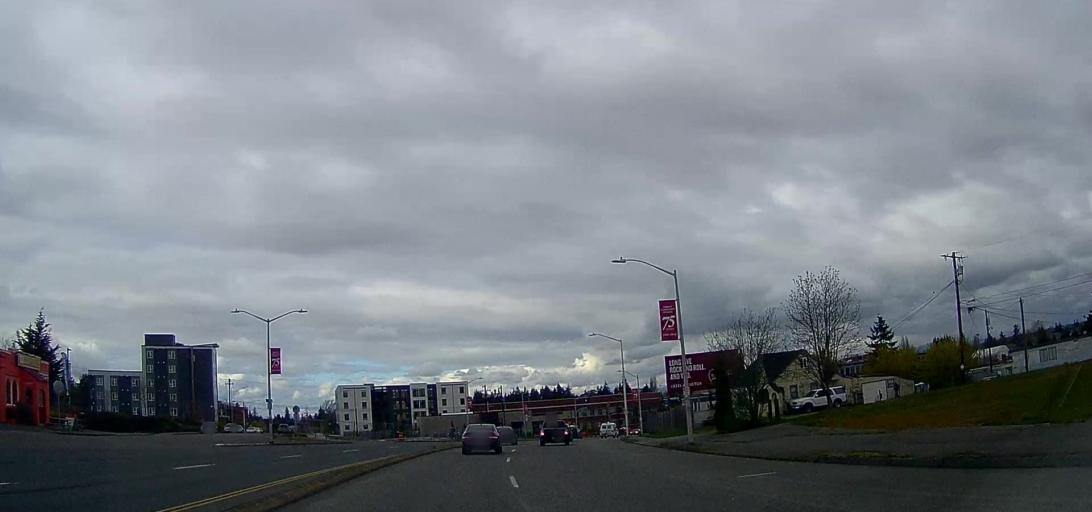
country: US
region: Washington
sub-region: Snohomish County
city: Everett
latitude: 48.0026
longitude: -122.2008
